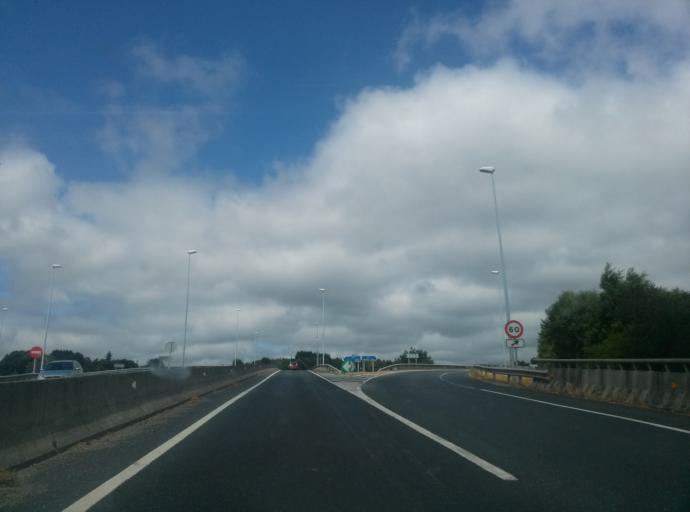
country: ES
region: Galicia
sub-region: Provincia de Lugo
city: Lugo
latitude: 43.0565
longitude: -7.5616
